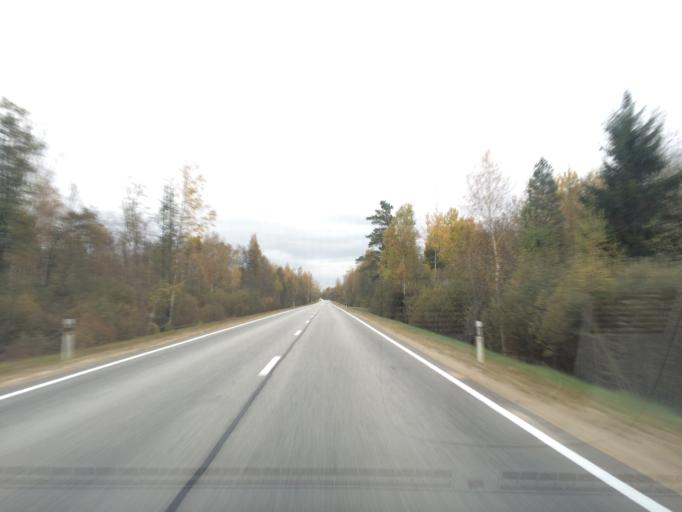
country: LV
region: Livani
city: Livani
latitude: 56.5306
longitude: 26.3553
